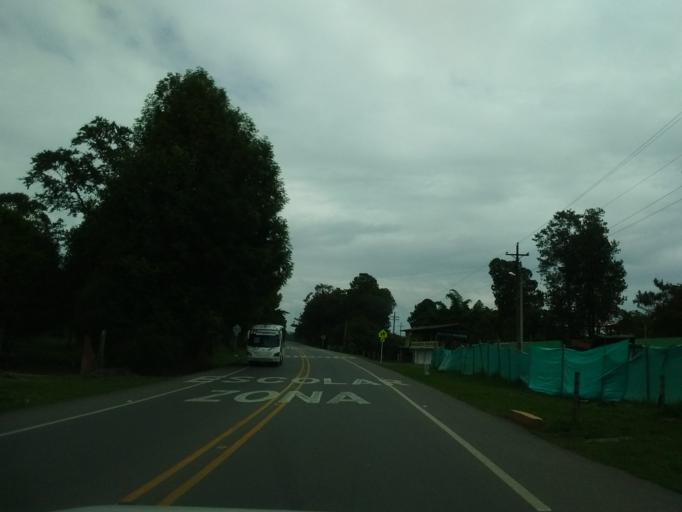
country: CO
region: Cauca
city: Cajibio
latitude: 2.5746
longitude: -76.5551
